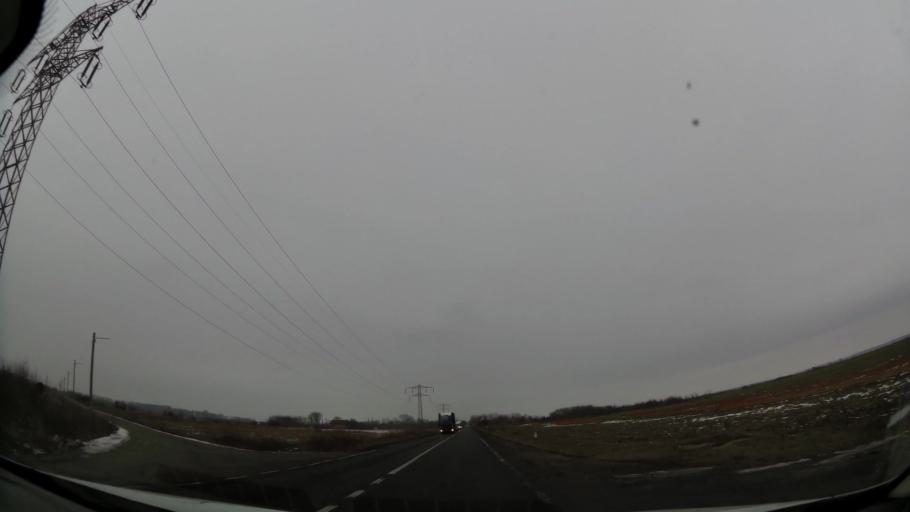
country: RO
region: Dambovita
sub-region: Comuna Contesti
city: Balteni
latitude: 44.6675
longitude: 25.6634
